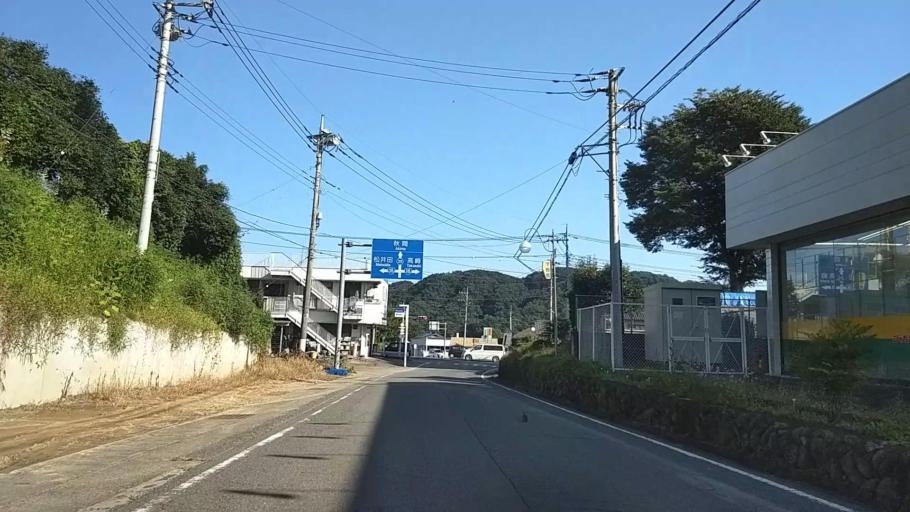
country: JP
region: Gunma
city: Annaka
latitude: 36.3325
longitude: 138.9008
